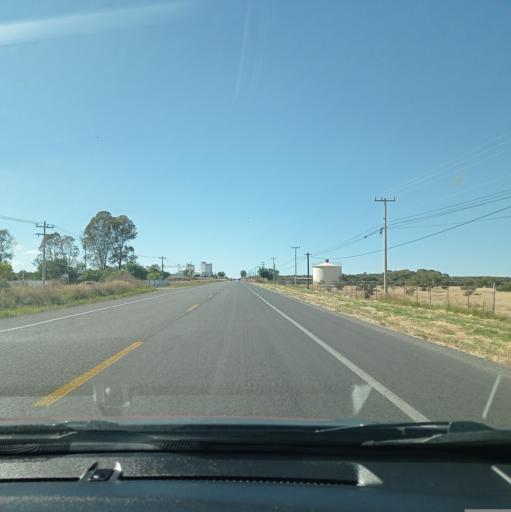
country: MX
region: Jalisco
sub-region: San Julian
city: Colonia Veintitres de Mayo
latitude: 21.0117
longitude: -102.2117
